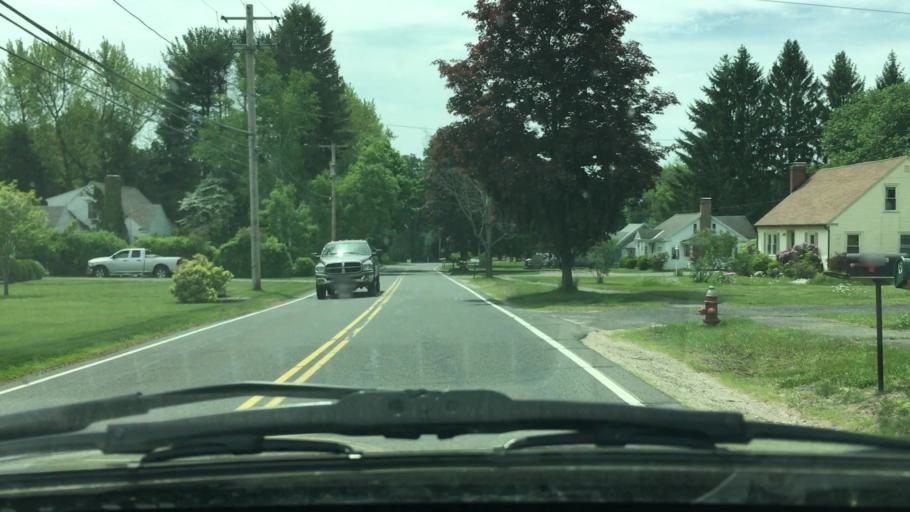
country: US
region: Massachusetts
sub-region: Hampshire County
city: Belchertown
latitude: 42.2708
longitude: -72.3980
